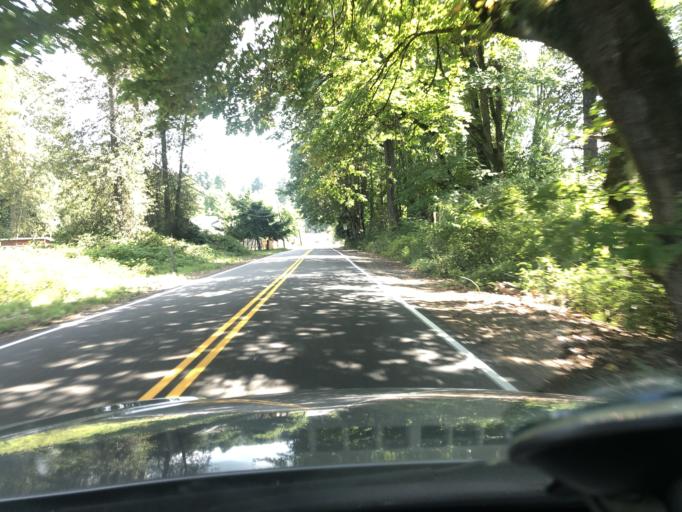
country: US
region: Washington
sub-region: King County
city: Lea Hill
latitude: 47.3280
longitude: -122.2076
